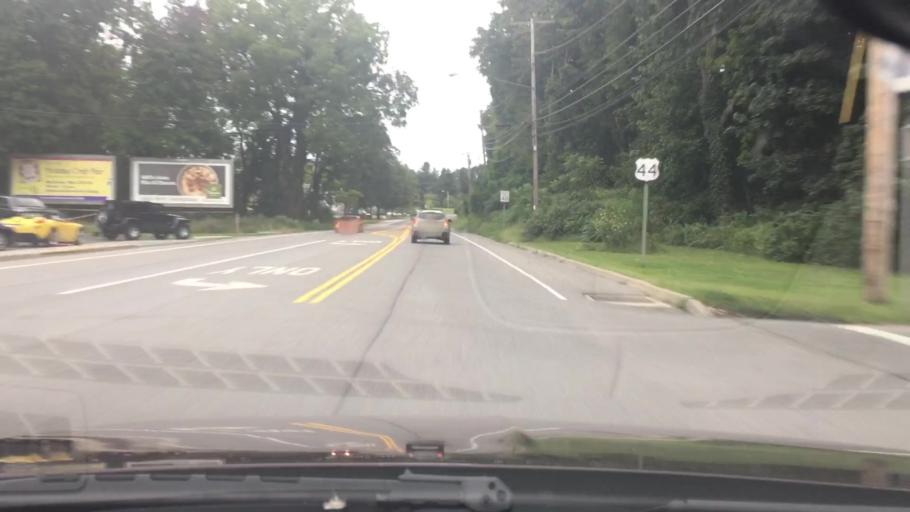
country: US
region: New York
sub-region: Dutchess County
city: Pleasant Valley
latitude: 41.7282
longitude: -73.8404
